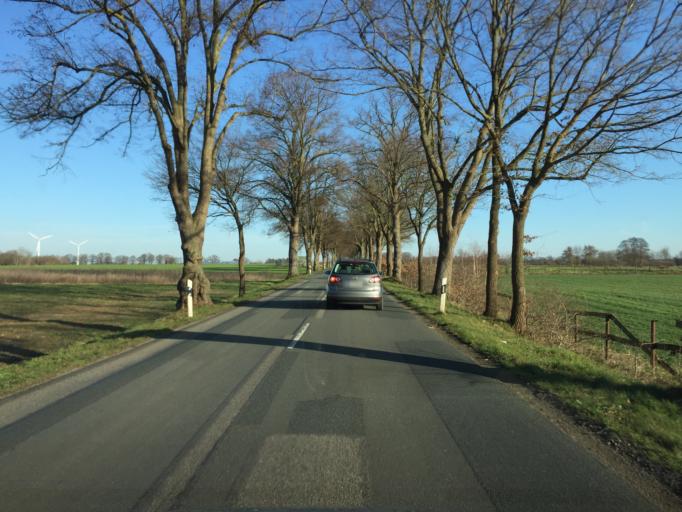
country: DE
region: Lower Saxony
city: Linsburg
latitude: 52.5783
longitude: 9.2772
